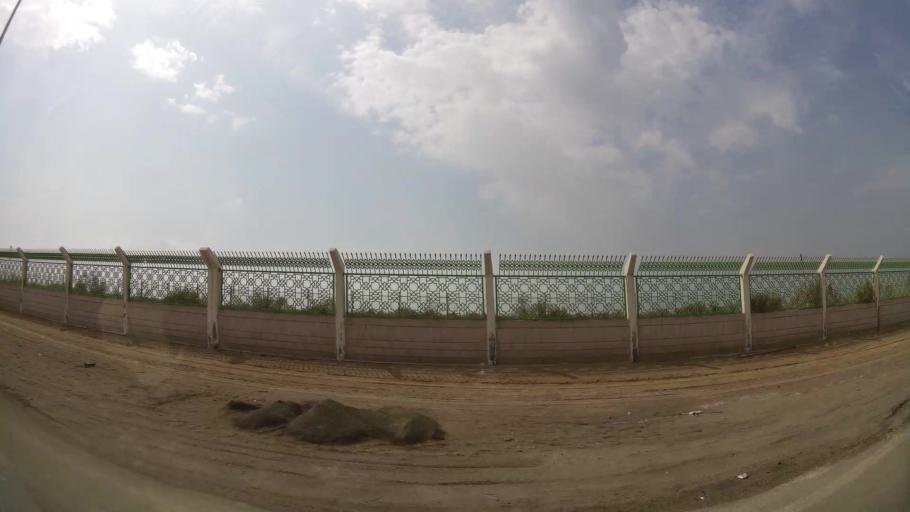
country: AE
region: Abu Dhabi
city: Abu Dhabi
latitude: 24.5300
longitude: 54.6394
